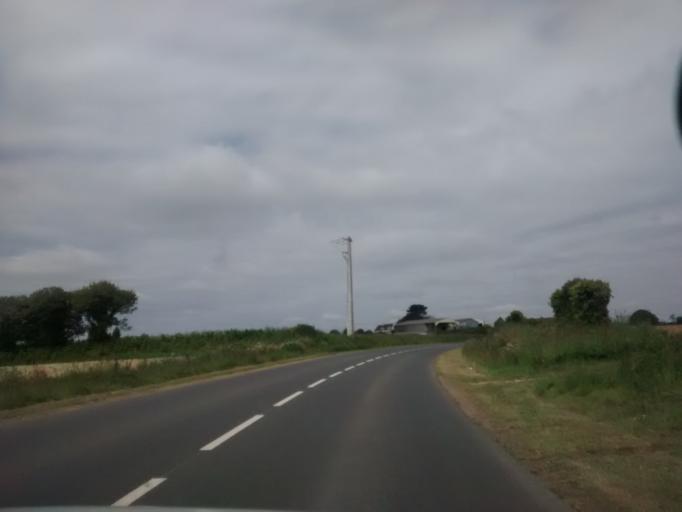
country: FR
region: Brittany
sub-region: Departement des Cotes-d'Armor
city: Penvenan
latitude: 48.7813
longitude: -3.3198
